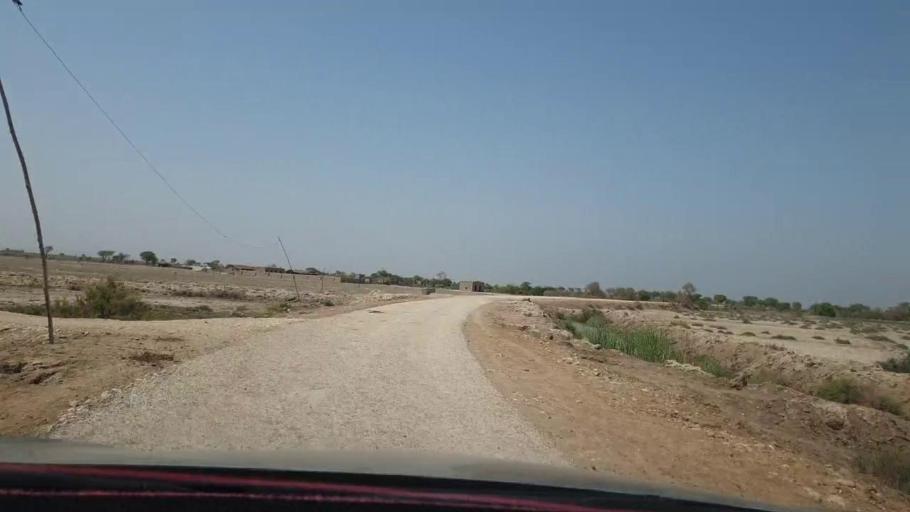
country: PK
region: Sindh
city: Warah
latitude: 27.5062
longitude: 67.7052
